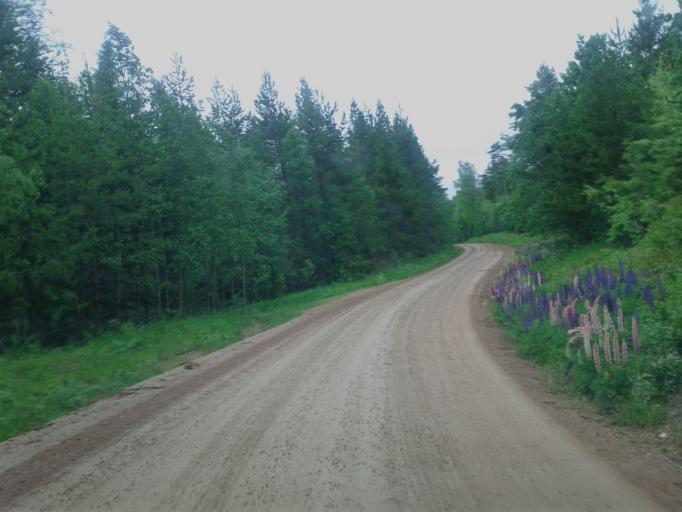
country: SE
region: Gaevleborg
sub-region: Hudiksvalls Kommun
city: Delsbo
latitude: 62.1668
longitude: 16.5393
